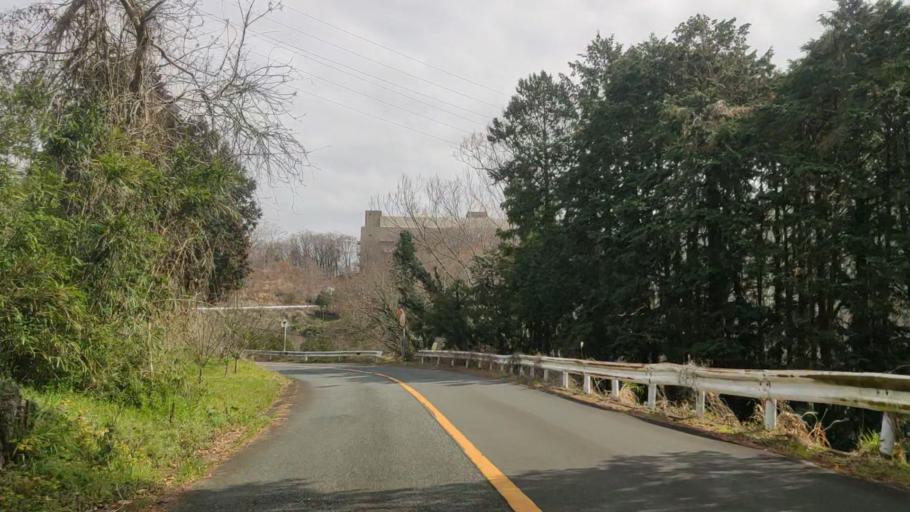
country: JP
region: Kanagawa
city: Hadano
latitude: 35.3364
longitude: 139.2241
